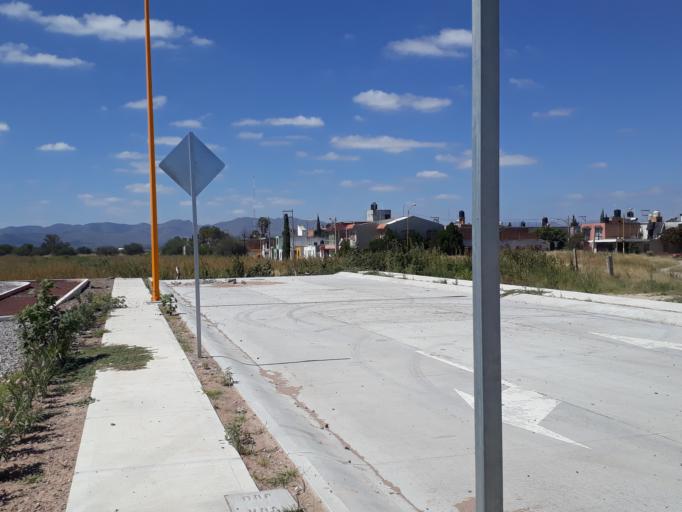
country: MX
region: Aguascalientes
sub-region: Aguascalientes
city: San Sebastian [Fraccionamiento]
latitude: 21.8385
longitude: -102.2974
